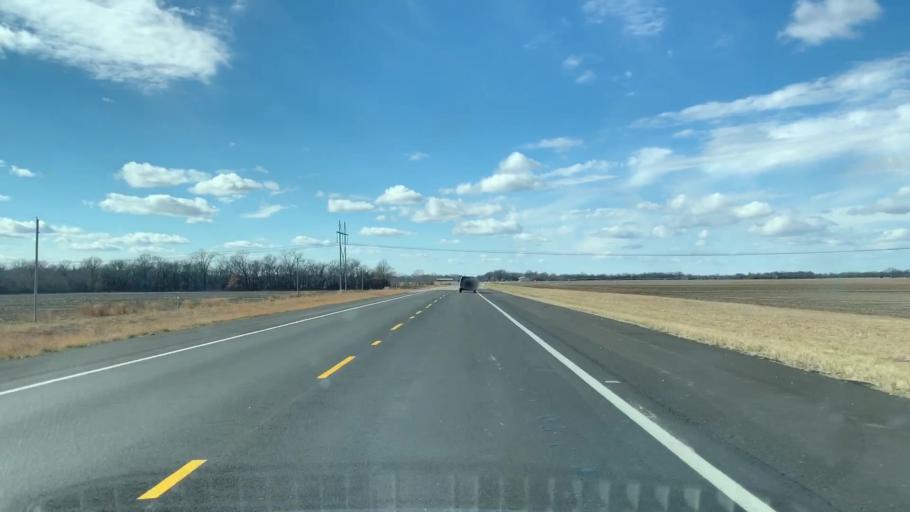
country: US
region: Kansas
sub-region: Labette County
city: Parsons
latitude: 37.3403
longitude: -95.1144
